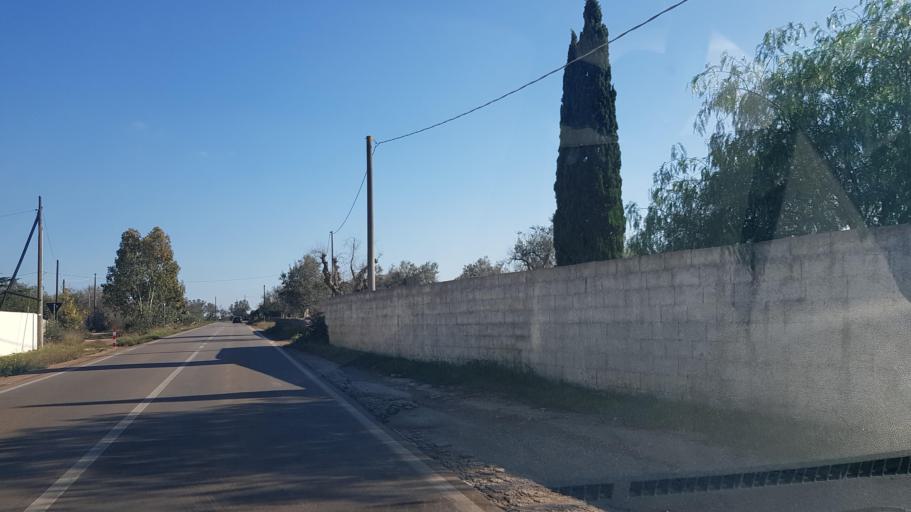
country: IT
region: Apulia
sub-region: Provincia di Lecce
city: Montesano Salentino
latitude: 39.9642
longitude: 18.3335
